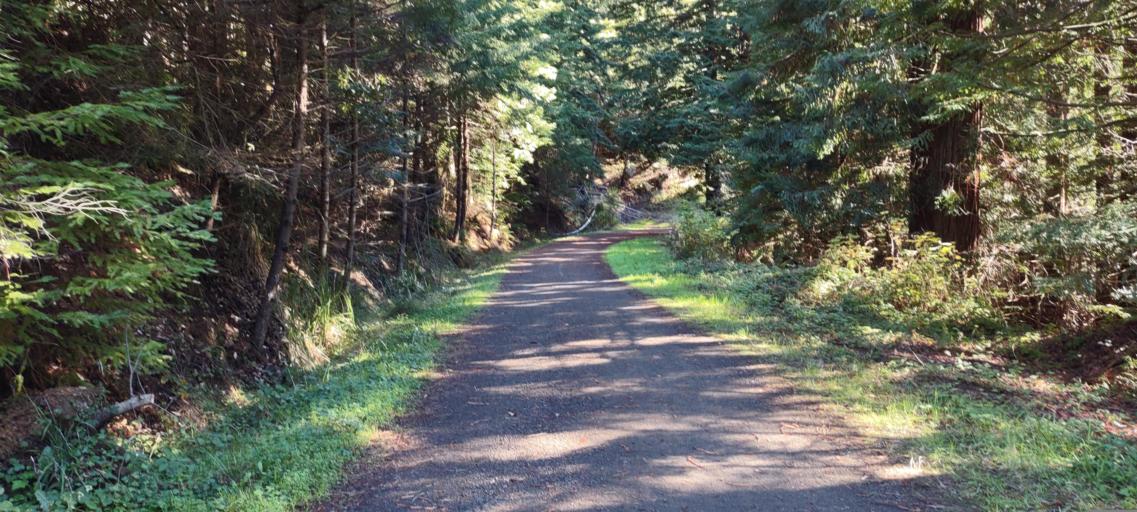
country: US
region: California
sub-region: Mendocino County
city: Fort Bragg
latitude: 39.3022
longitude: -123.7648
